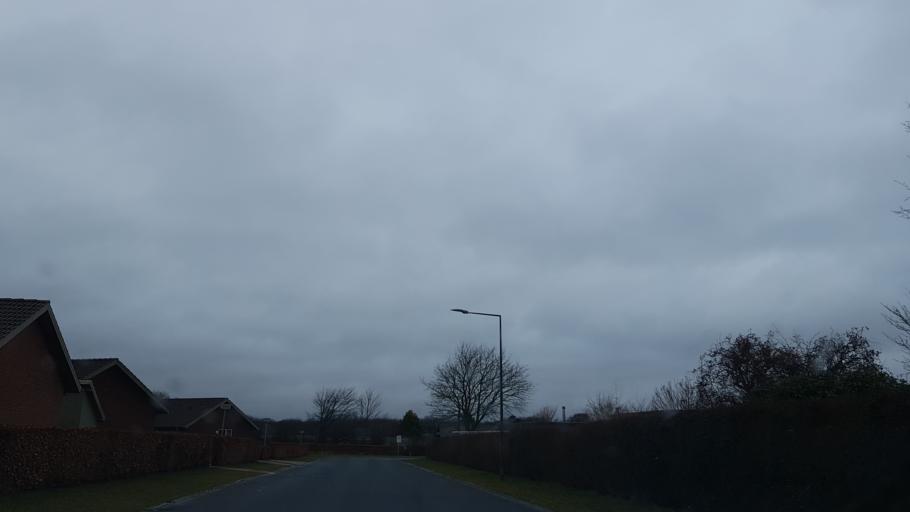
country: DK
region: South Denmark
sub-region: Kolding Kommune
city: Vamdrup
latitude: 55.3579
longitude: 9.1956
